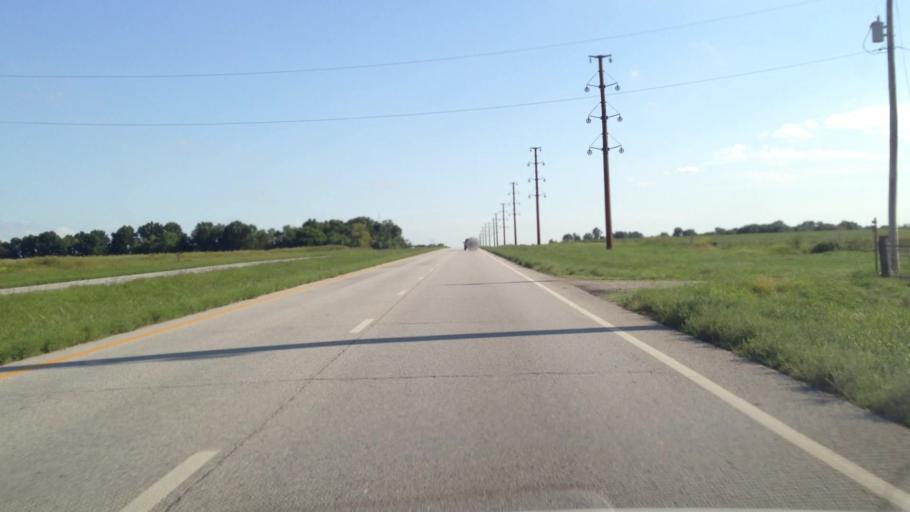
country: US
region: Kansas
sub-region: Crawford County
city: Frontenac
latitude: 37.4969
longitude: -94.7053
